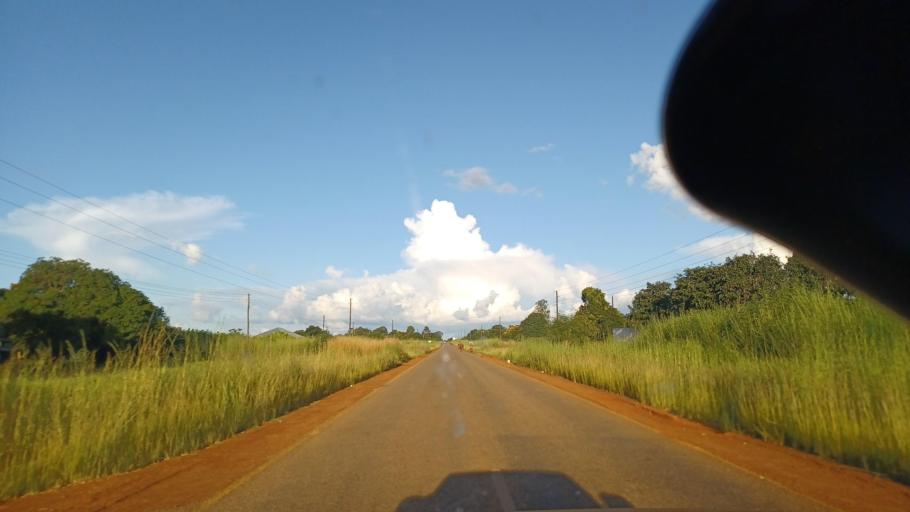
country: ZM
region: North-Western
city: Kalengwa
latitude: -13.1431
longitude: 25.0355
